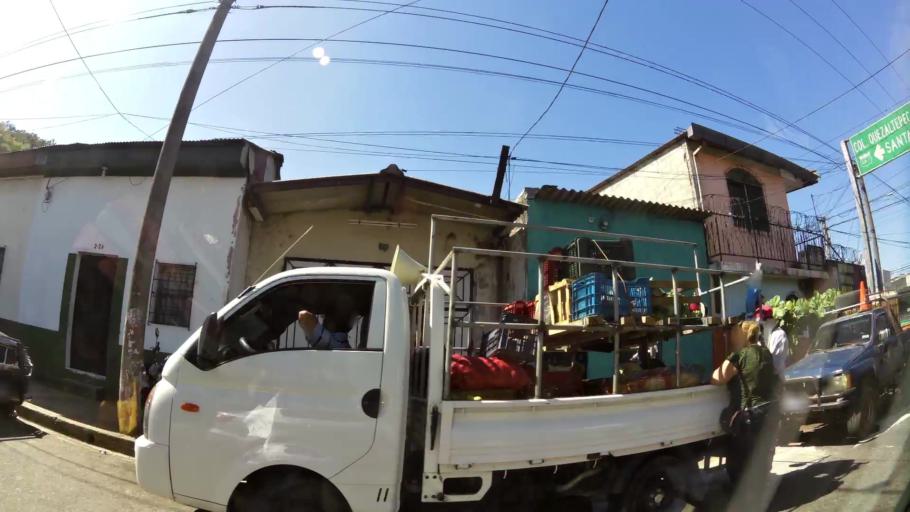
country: SV
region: La Libertad
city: Santa Tecla
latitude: 13.6733
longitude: -89.2949
